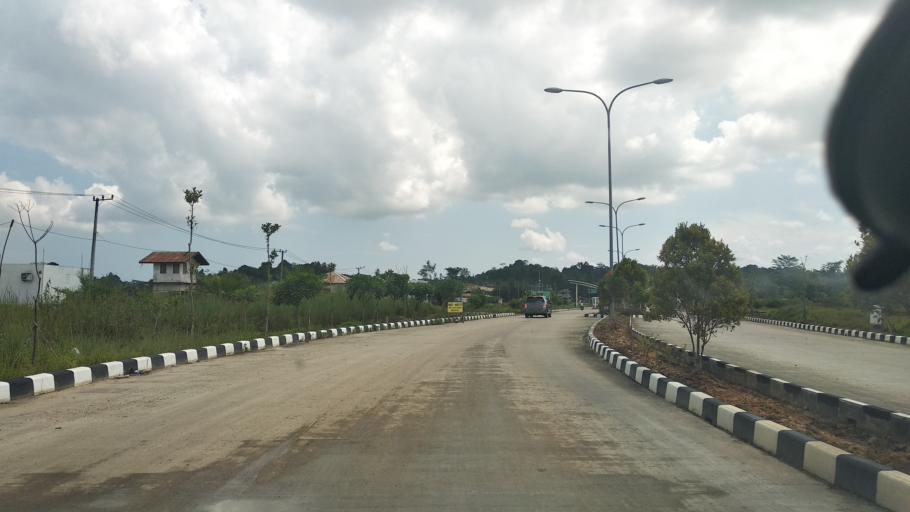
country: ID
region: East Kalimantan
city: Samarinda
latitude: -0.3722
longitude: 117.2613
